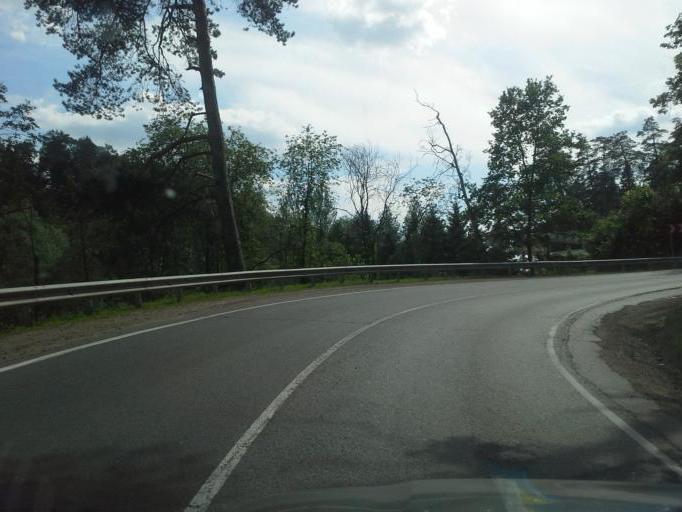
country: RU
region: Moskovskaya
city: Gorki Vtoryye
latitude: 55.7199
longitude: 37.1915
